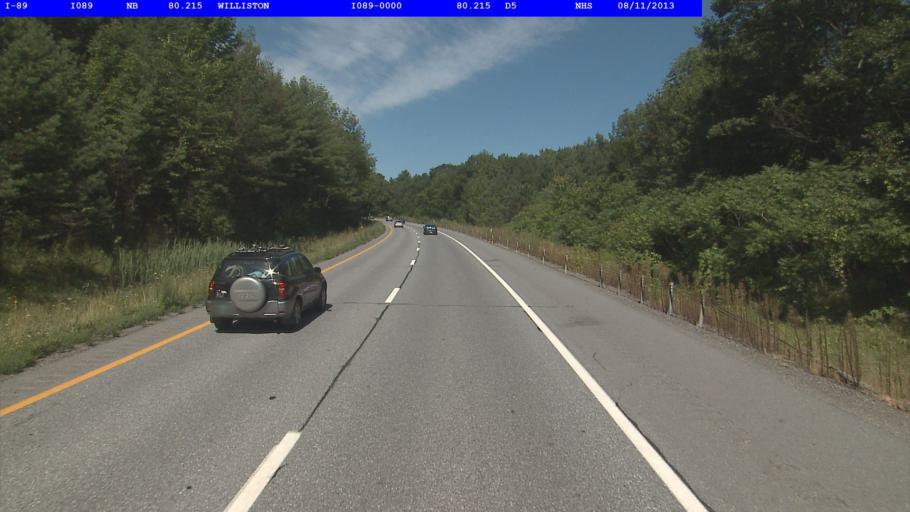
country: US
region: Vermont
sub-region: Chittenden County
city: Williston
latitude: 44.4321
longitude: -73.0403
